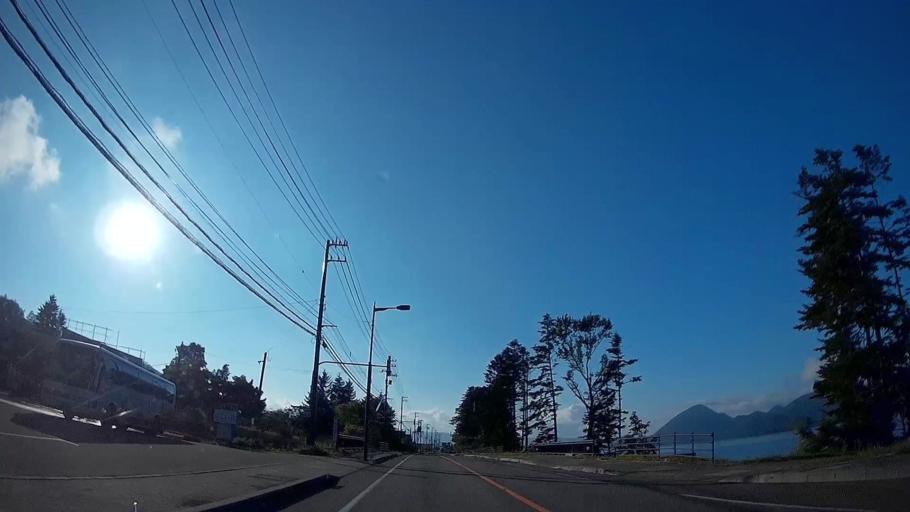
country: JP
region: Hokkaido
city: Date
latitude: 42.5566
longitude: 140.8565
